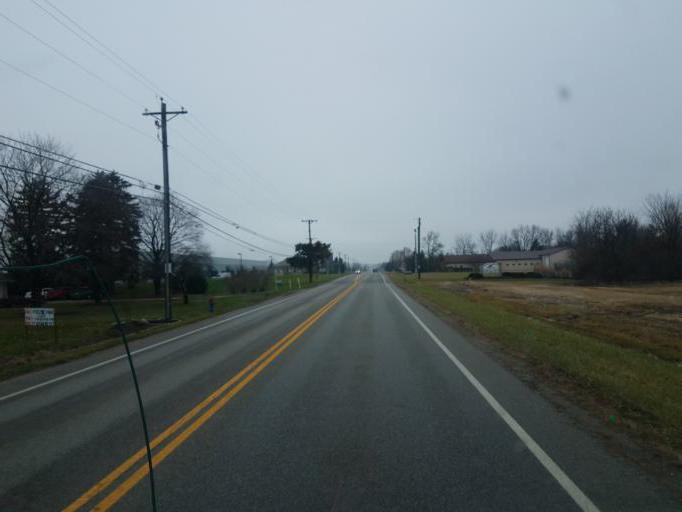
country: US
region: Ohio
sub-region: Union County
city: New California
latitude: 40.1282
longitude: -83.1987
